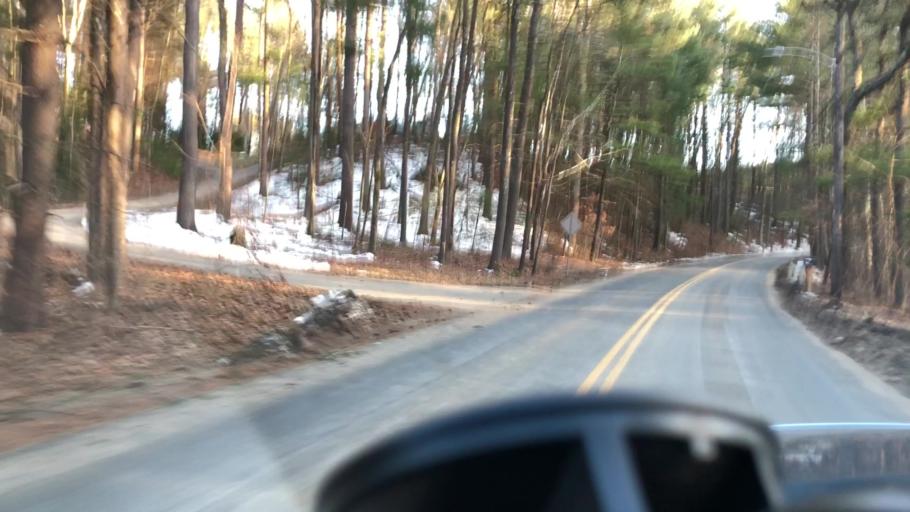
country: US
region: Massachusetts
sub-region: Hampshire County
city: Southampton
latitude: 42.2102
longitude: -72.6794
